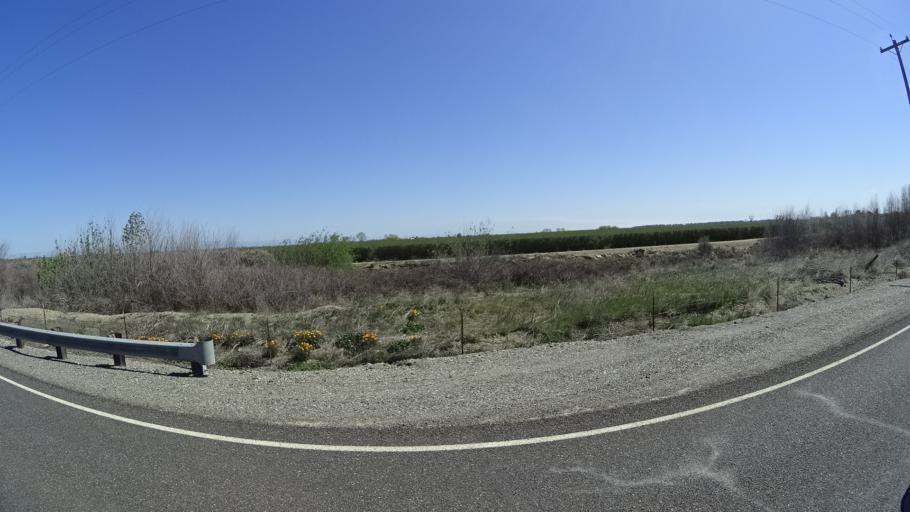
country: US
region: California
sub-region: Glenn County
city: Willows
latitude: 39.6170
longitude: -122.2500
